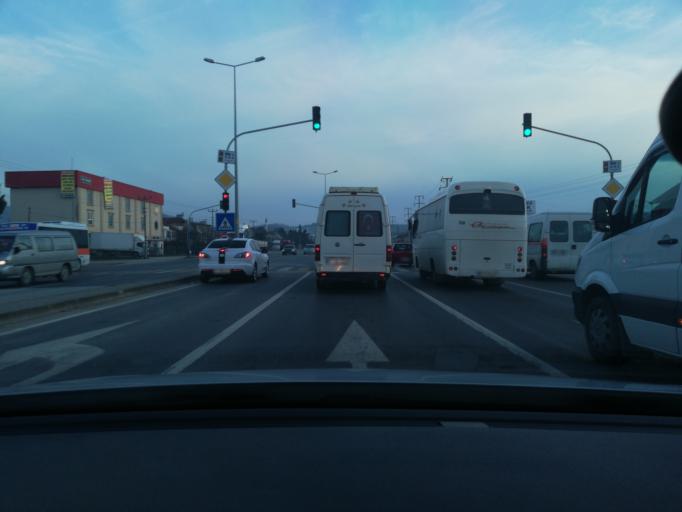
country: TR
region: Duzce
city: Duzce
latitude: 40.8760
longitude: 31.1697
